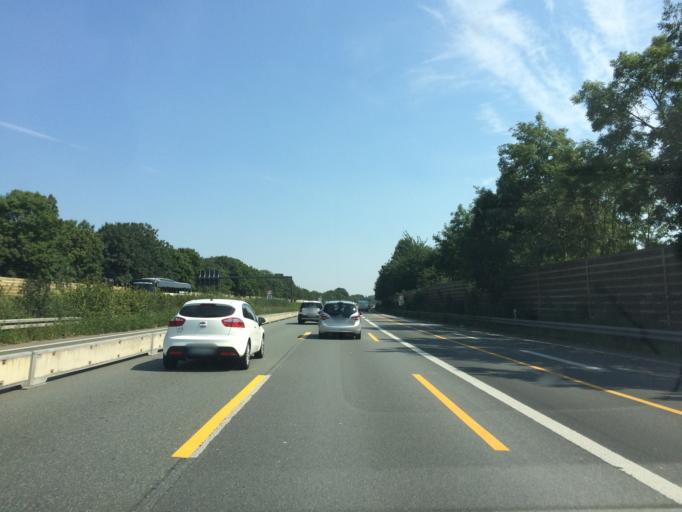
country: DE
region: North Rhine-Westphalia
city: Lunen
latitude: 51.5787
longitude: 7.5003
